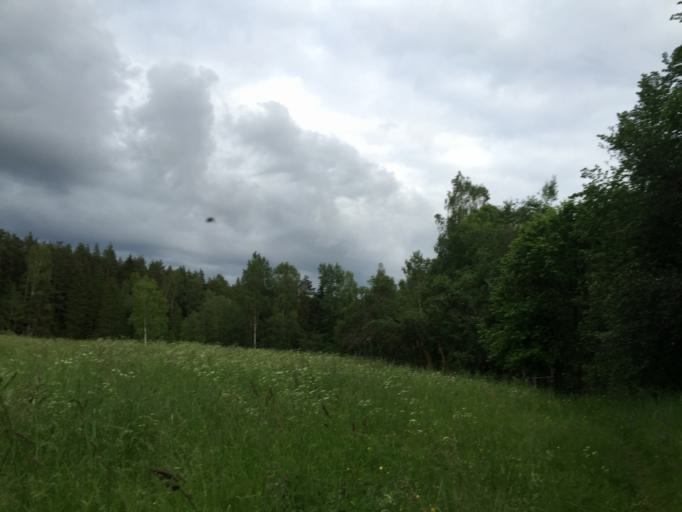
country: LV
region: Ligatne
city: Ligatne
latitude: 57.2385
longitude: 25.1528
